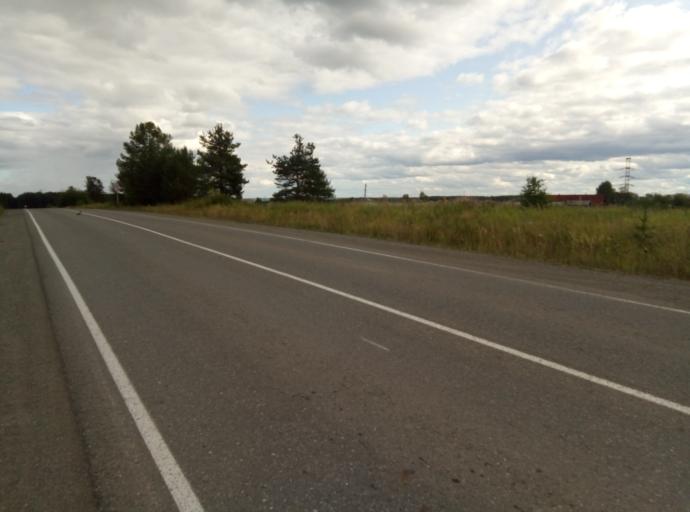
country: RU
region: Sverdlovsk
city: Karpinsk
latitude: 59.7868
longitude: 59.9990
